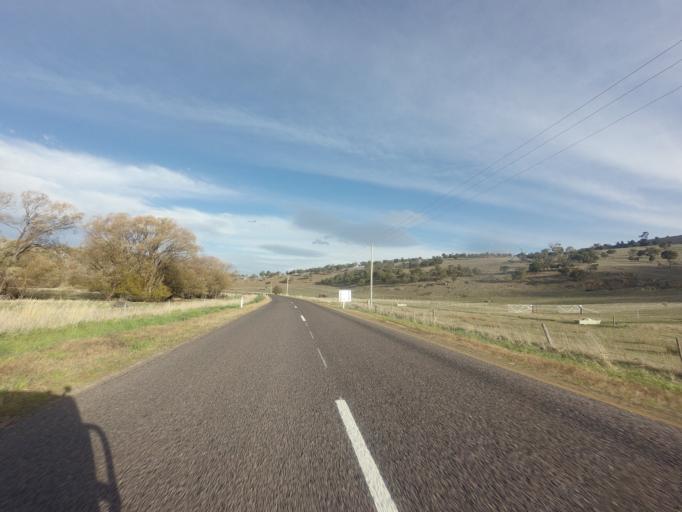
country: AU
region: Tasmania
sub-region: Brighton
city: Bridgewater
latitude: -42.4333
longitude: 147.1439
